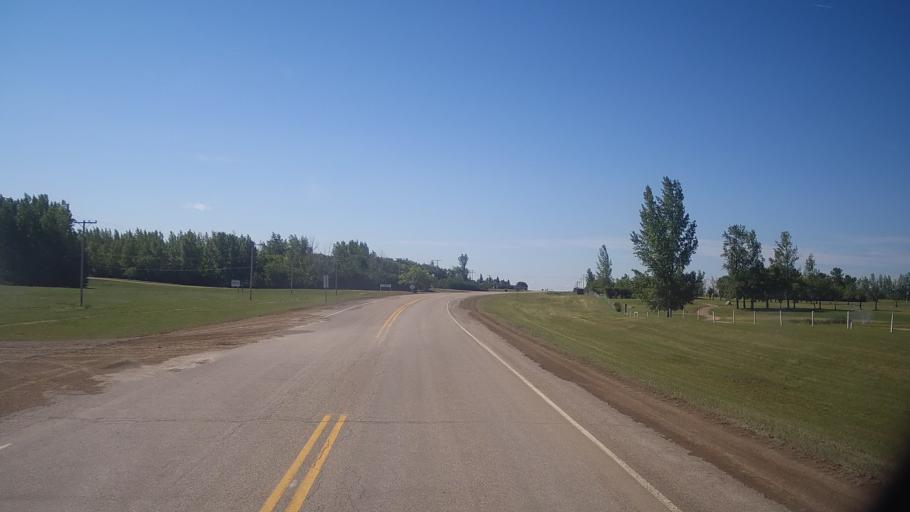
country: CA
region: Saskatchewan
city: Watrous
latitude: 51.7177
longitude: -105.4515
